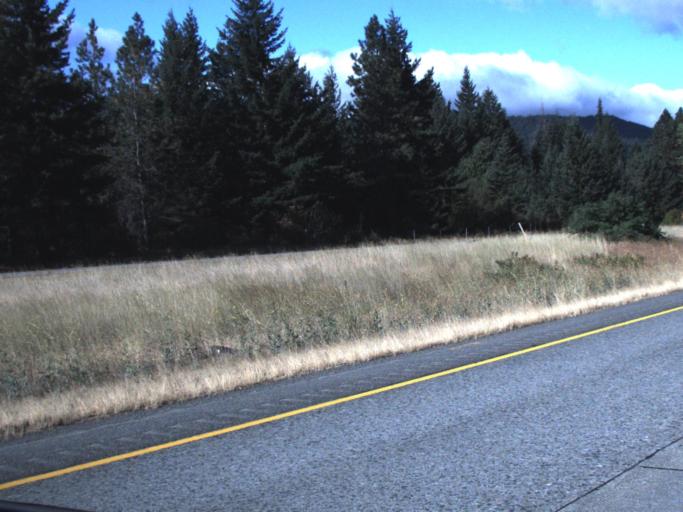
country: US
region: Washington
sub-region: Kittitas County
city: Cle Elum
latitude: 47.2141
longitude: -121.1103
